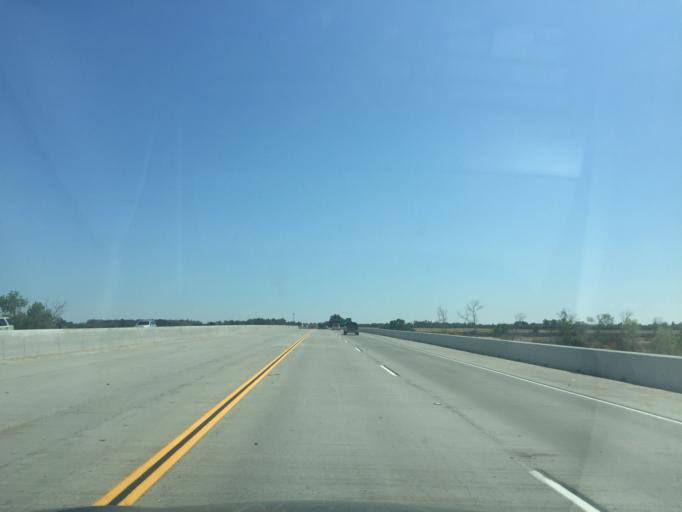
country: US
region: California
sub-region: Tehama County
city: Corning
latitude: 39.9767
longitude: -122.2021
